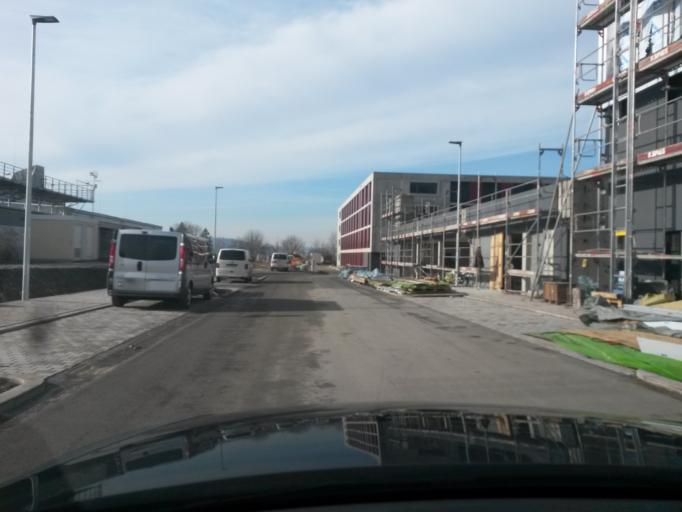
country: DE
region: Bavaria
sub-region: Regierungsbezirk Unterfranken
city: Wuerzburg
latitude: 49.7867
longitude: 9.9682
